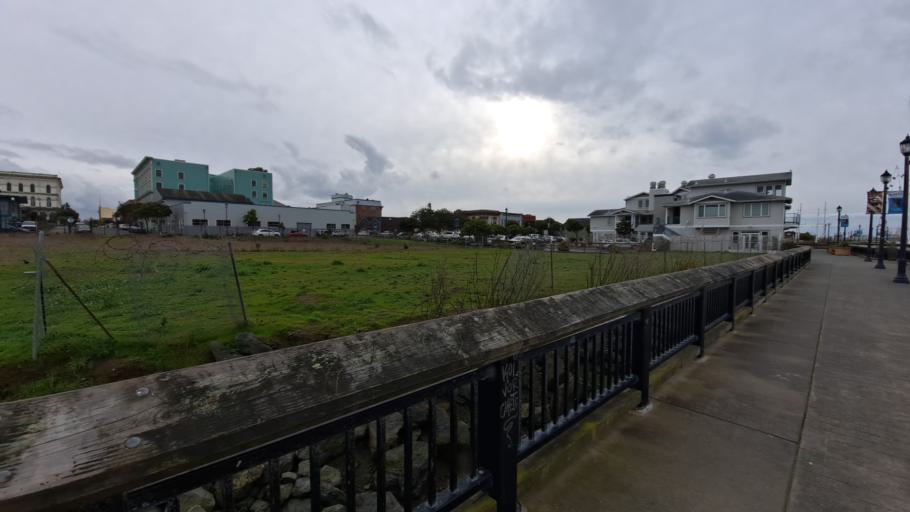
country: US
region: California
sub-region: Humboldt County
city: Eureka
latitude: 40.8061
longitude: -124.1659
